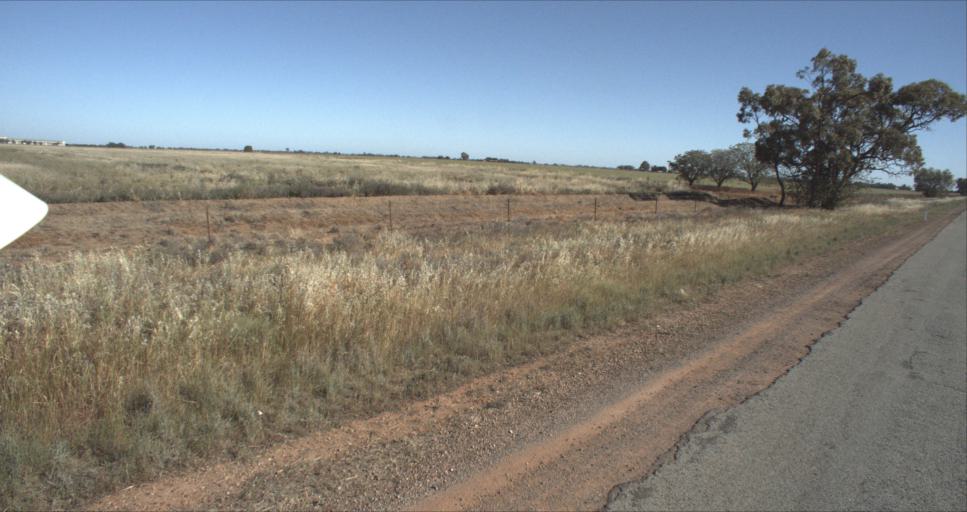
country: AU
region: New South Wales
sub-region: Leeton
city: Leeton
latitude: -34.5610
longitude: 146.3127
